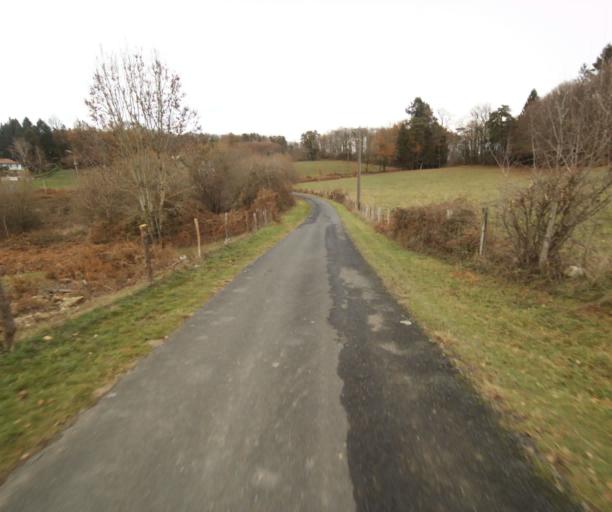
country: FR
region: Limousin
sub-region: Departement de la Correze
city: Saint-Mexant
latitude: 45.2554
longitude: 1.6561
